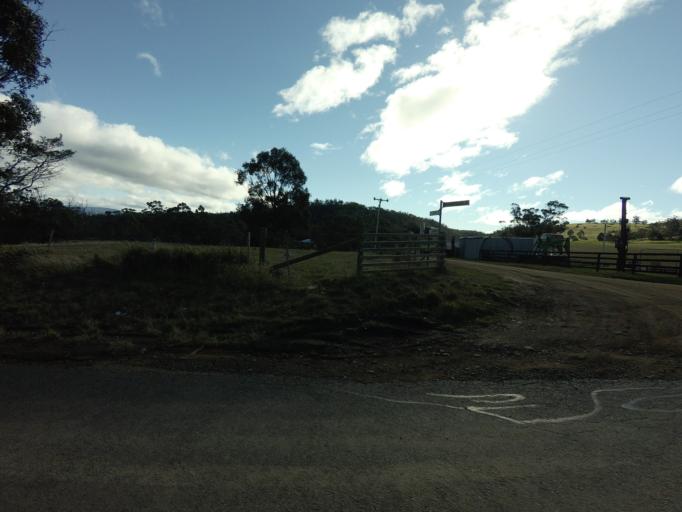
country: AU
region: Tasmania
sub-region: Derwent Valley
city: New Norfolk
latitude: -42.7260
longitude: 147.0311
